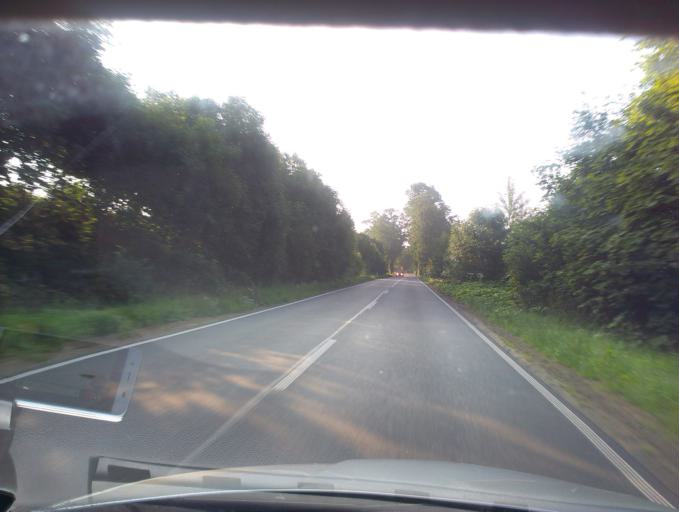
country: PL
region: West Pomeranian Voivodeship
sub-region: Powiat szczecinecki
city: Barwice
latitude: 53.7251
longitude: 16.3895
